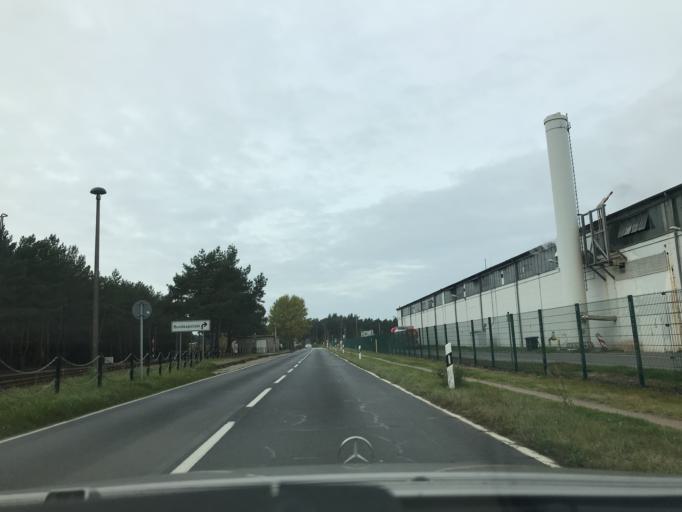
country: DE
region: Mecklenburg-Vorpommern
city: Lubmin
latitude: 54.1382
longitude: 13.6573
